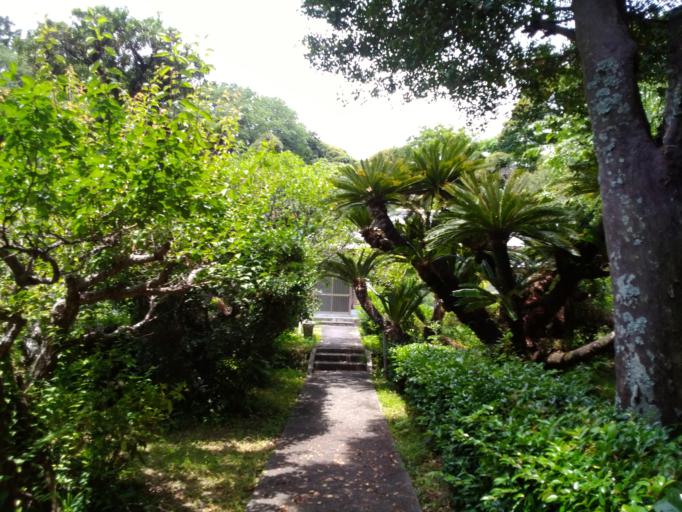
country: JP
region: Shizuoka
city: Kakegawa
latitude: 34.7380
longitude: 138.0373
